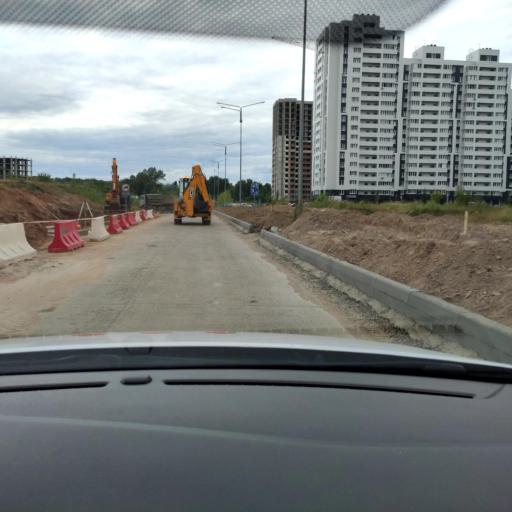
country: RU
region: Tatarstan
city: Osinovo
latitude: 55.8443
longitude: 48.9099
